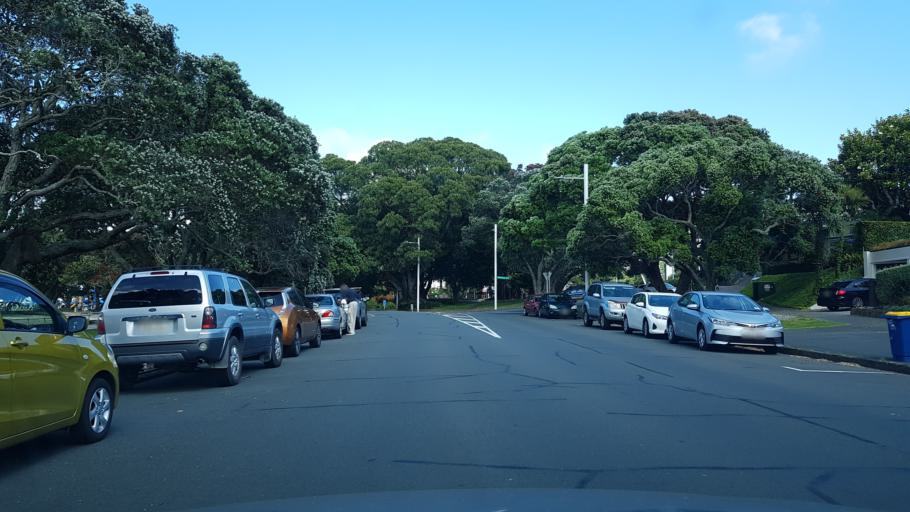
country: NZ
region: Auckland
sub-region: Auckland
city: Auckland
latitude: -36.8316
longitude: 174.7996
